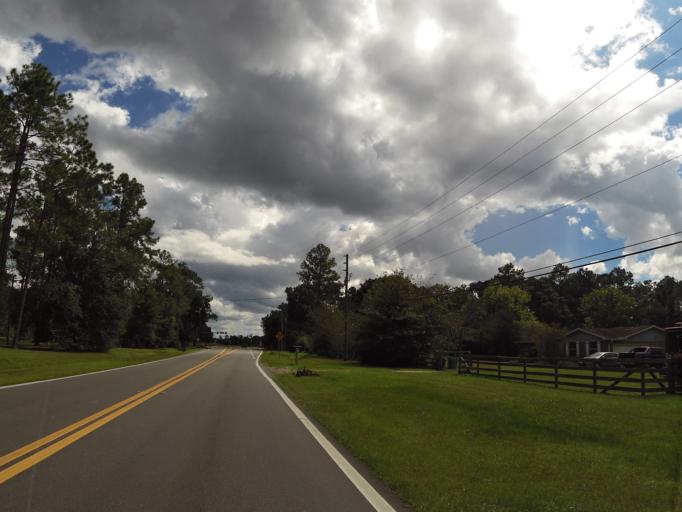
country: US
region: Florida
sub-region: Saint Johns County
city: Saint Augustine
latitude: 29.9329
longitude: -81.4945
